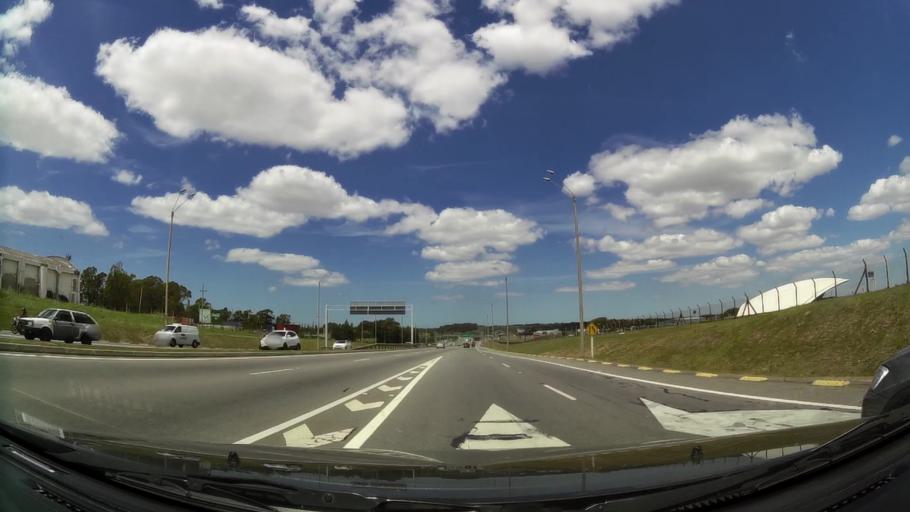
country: UY
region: Canelones
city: Colonia Nicolich
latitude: -34.8340
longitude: -56.0119
